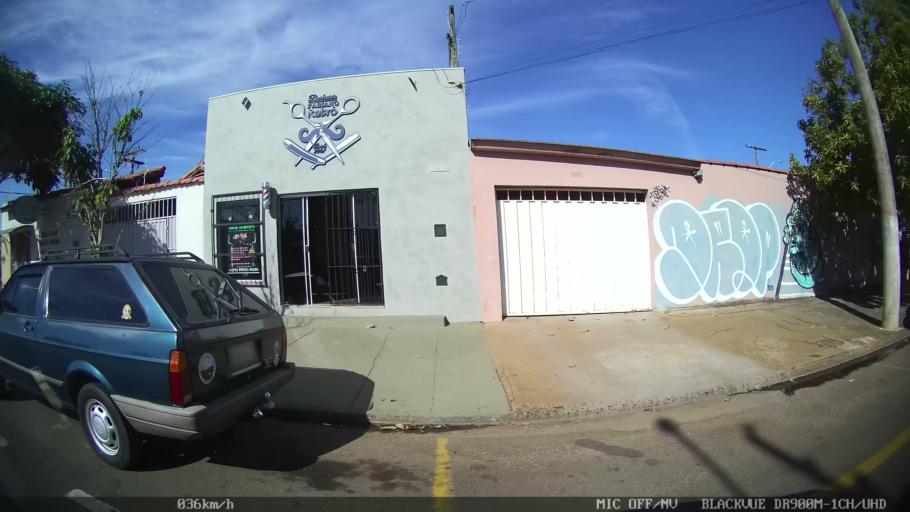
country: BR
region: Sao Paulo
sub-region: Franca
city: Franca
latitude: -20.5014
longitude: -47.4142
